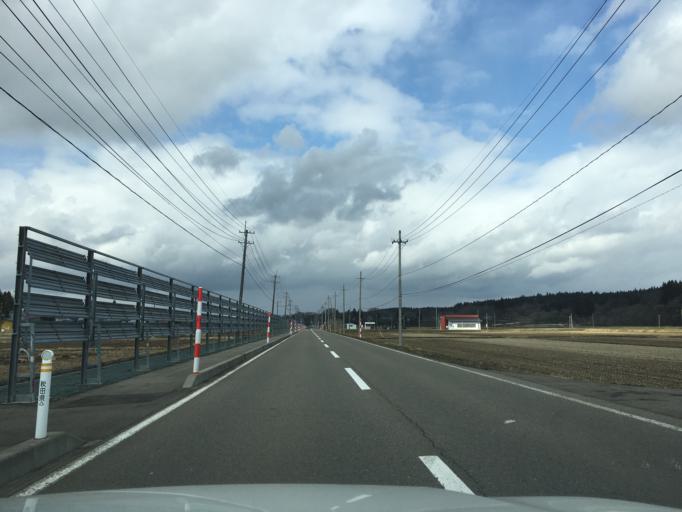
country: JP
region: Akita
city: Takanosu
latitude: 40.1357
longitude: 140.3545
